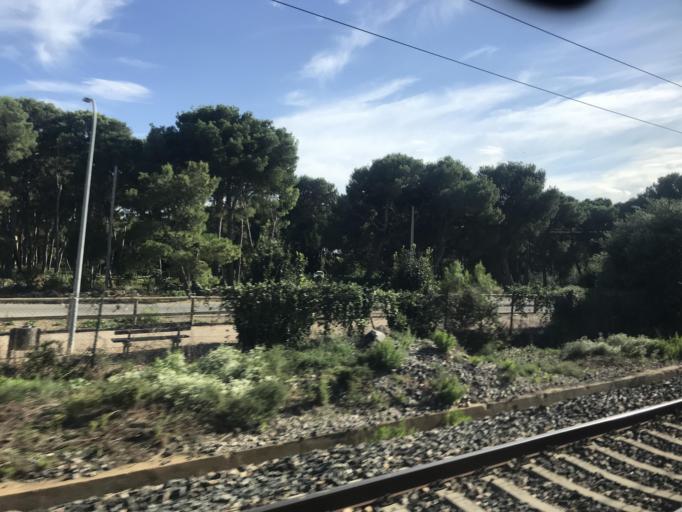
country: ES
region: Catalonia
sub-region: Provincia de Tarragona
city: Camarles
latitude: 40.7688
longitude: 0.6615
